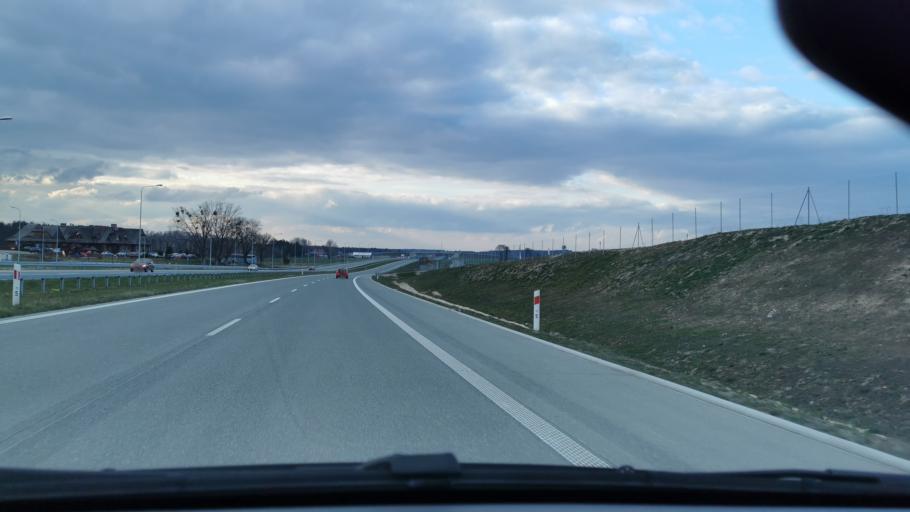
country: PL
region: Masovian Voivodeship
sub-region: Powiat garwolinski
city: Trojanow
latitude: 51.6745
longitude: 21.8679
